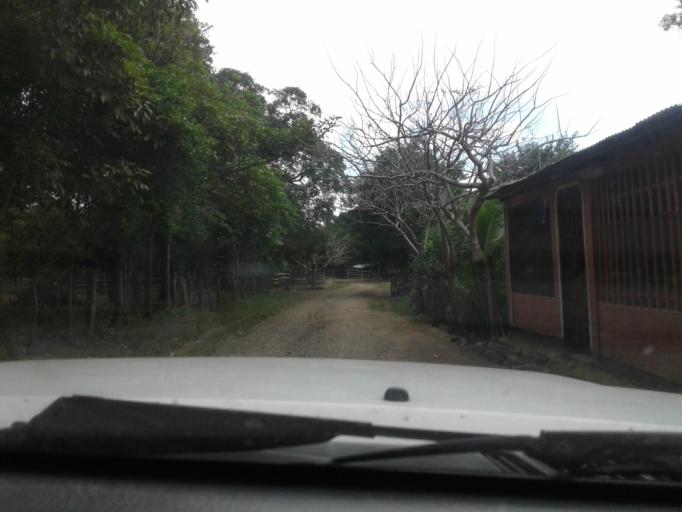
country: NI
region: Rivas
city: Belen
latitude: 11.6377
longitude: -85.9564
